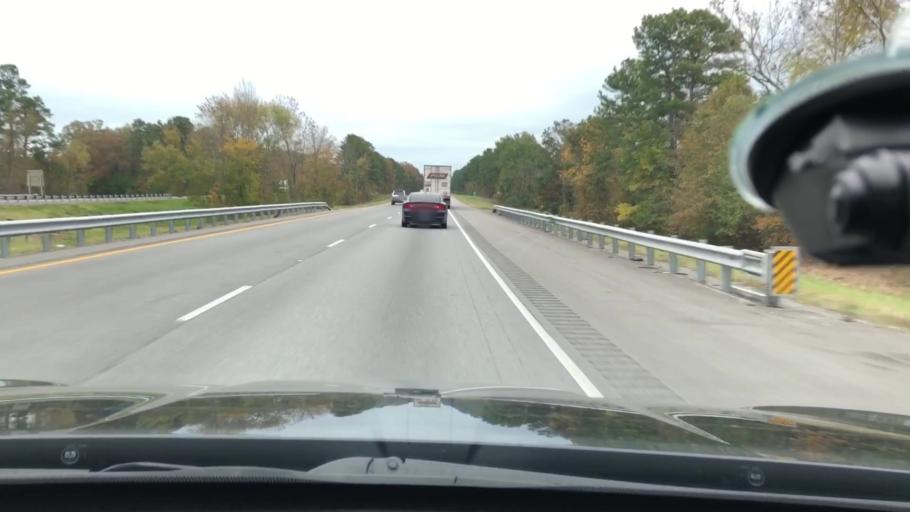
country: US
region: Arkansas
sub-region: Hempstead County
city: Hope
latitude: 33.6210
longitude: -93.7846
